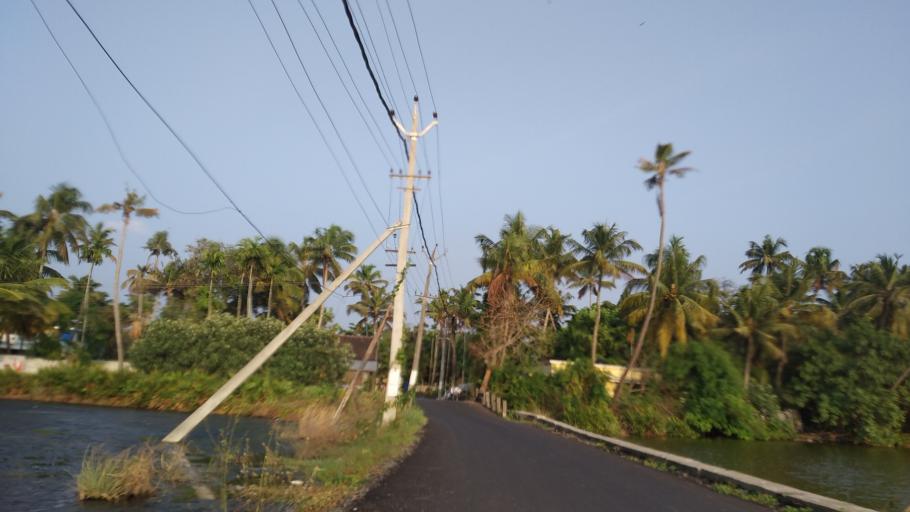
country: IN
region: Kerala
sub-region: Ernakulam
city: Elur
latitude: 10.1079
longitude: 76.1975
